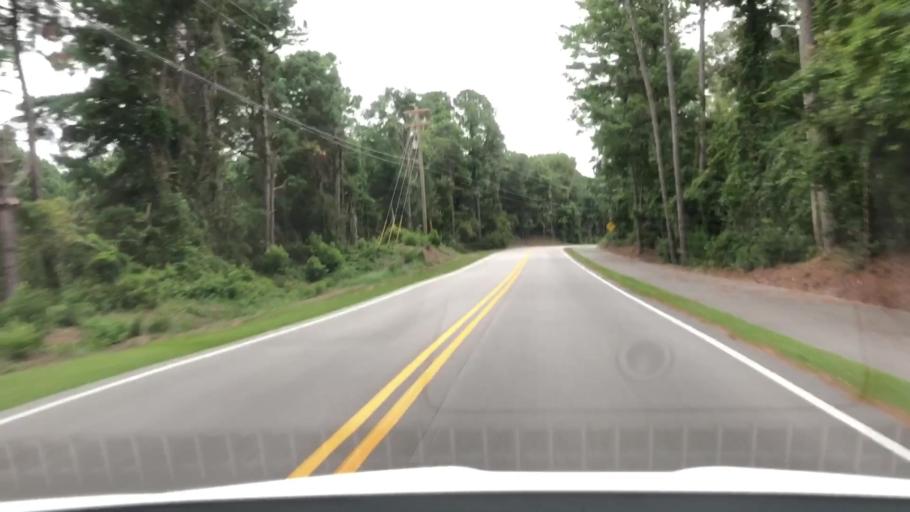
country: US
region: North Carolina
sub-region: Carteret County
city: Cedar Point
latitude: 34.6582
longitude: -77.0784
